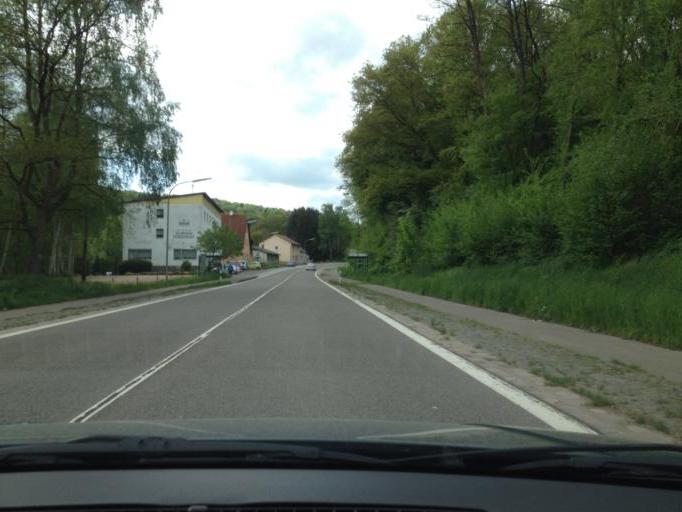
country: DE
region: Saarland
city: Ottweiler
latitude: 49.3862
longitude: 7.1769
